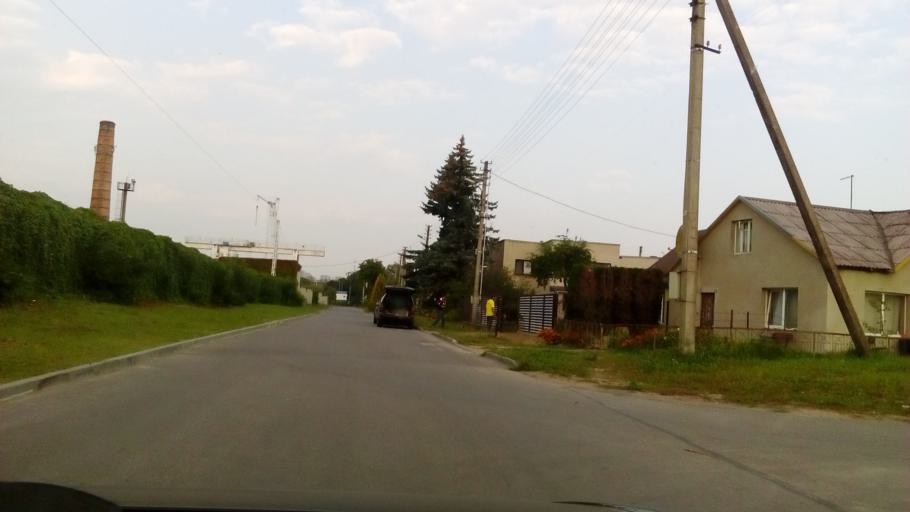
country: LT
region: Alytaus apskritis
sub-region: Alytus
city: Alytus
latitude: 54.3857
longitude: 24.0551
